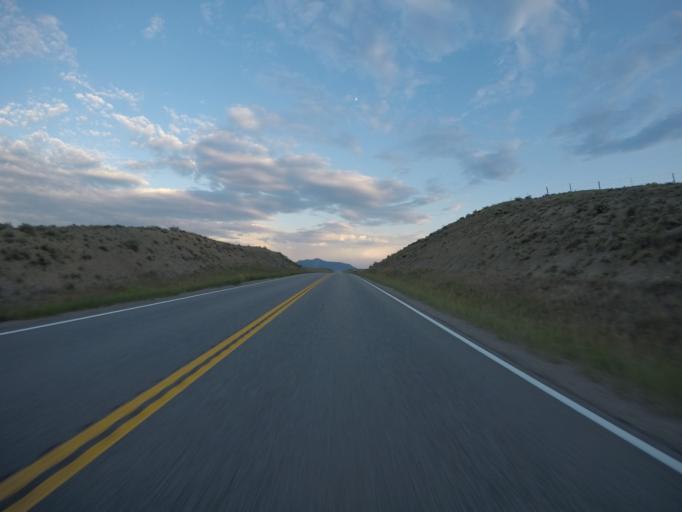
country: US
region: Colorado
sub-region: Grand County
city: Kremmling
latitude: 40.1843
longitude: -106.4233
